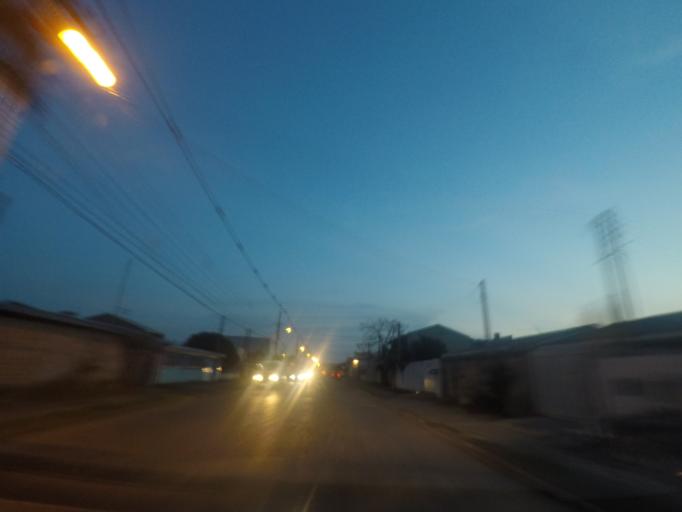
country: BR
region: Parana
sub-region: Pinhais
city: Pinhais
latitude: -25.4734
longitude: -49.1494
